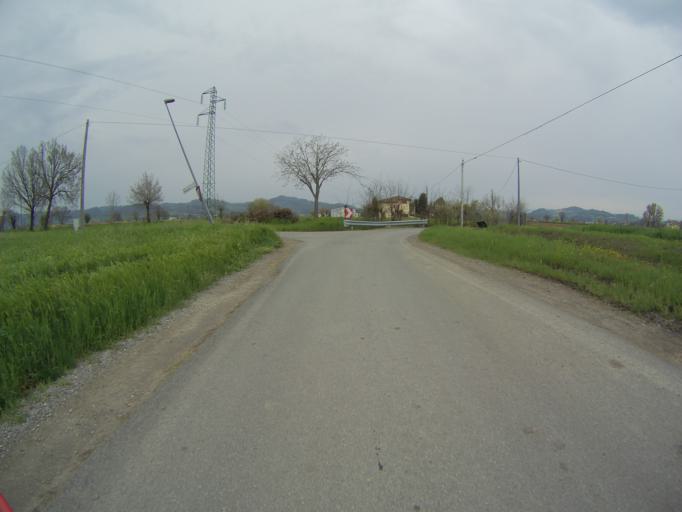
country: IT
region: Emilia-Romagna
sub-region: Provincia di Reggio Emilia
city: San Polo d'Enza
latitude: 44.6527
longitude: 10.4358
